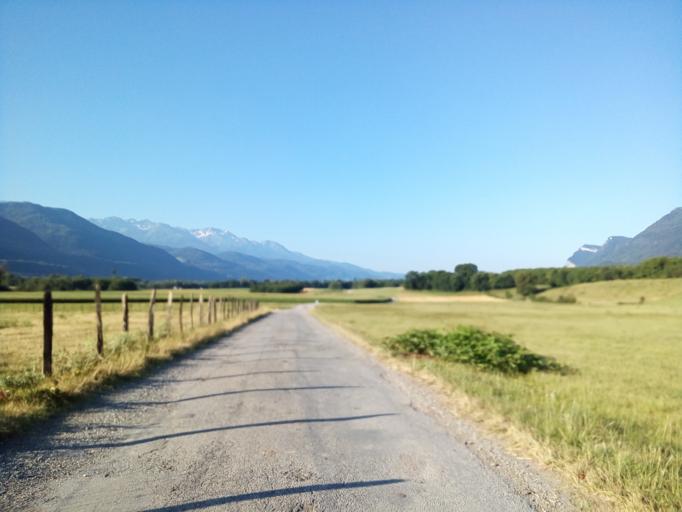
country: FR
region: Rhone-Alpes
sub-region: Departement de l'Isere
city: Saint-Vincent-de-Mercuze
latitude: 45.3748
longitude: 5.9723
